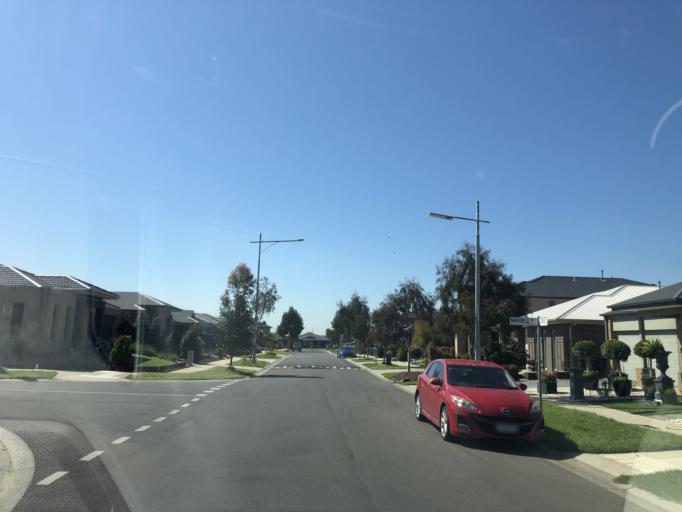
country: AU
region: Victoria
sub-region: Wyndham
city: Hoppers Crossing
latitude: -37.9030
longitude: 144.7211
